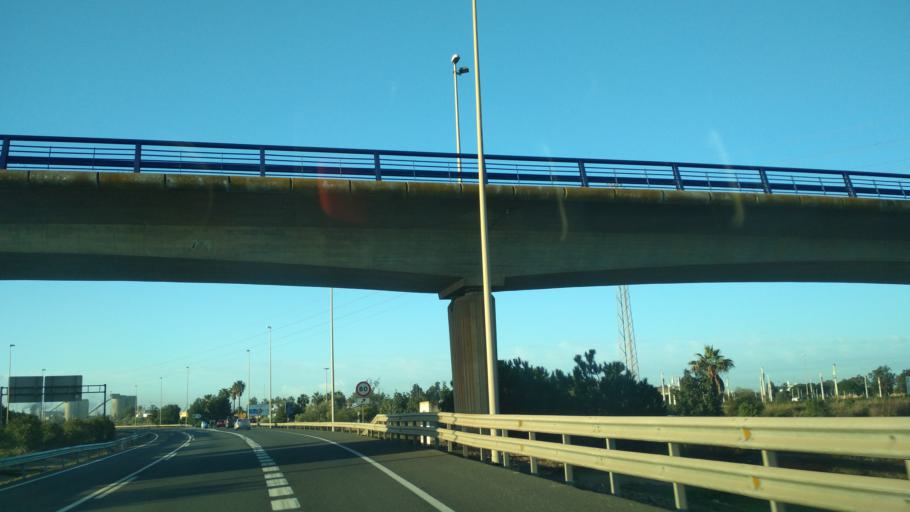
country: ES
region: Andalusia
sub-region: Provincia de Huelva
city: Huelva
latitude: 37.2458
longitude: -6.9437
